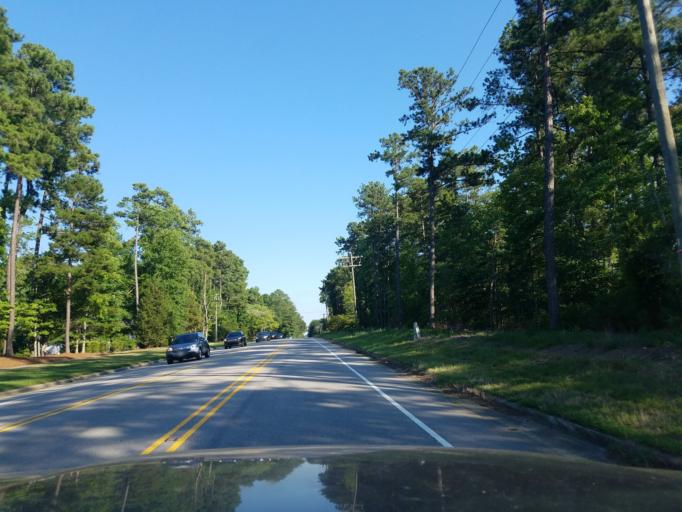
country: US
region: North Carolina
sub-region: Orange County
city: Chapel Hill
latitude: 35.8791
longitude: -78.9529
